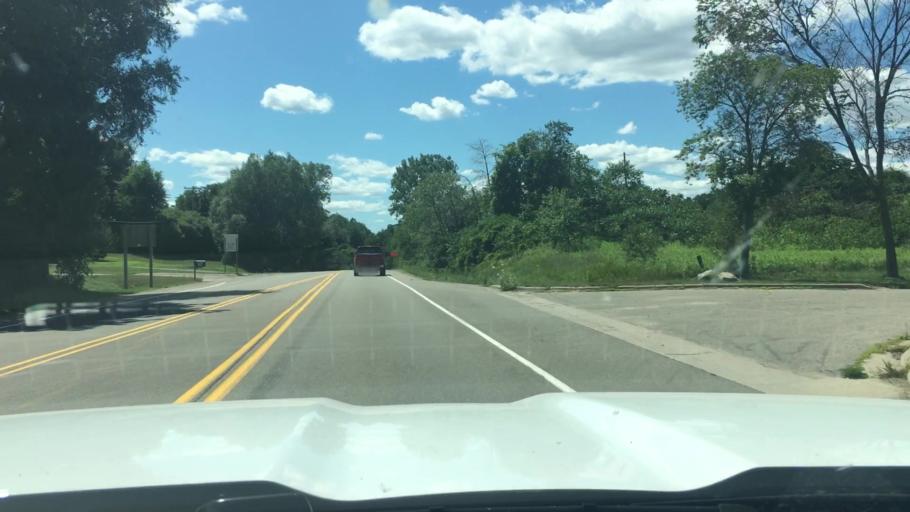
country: US
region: Michigan
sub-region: Kent County
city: Cedar Springs
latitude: 43.1756
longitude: -85.5822
